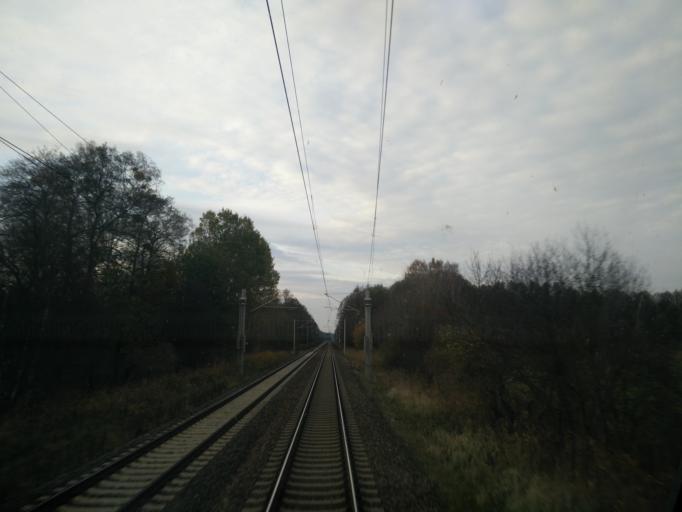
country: DE
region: Brandenburg
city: Gross Koris
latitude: 52.1375
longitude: 13.6710
